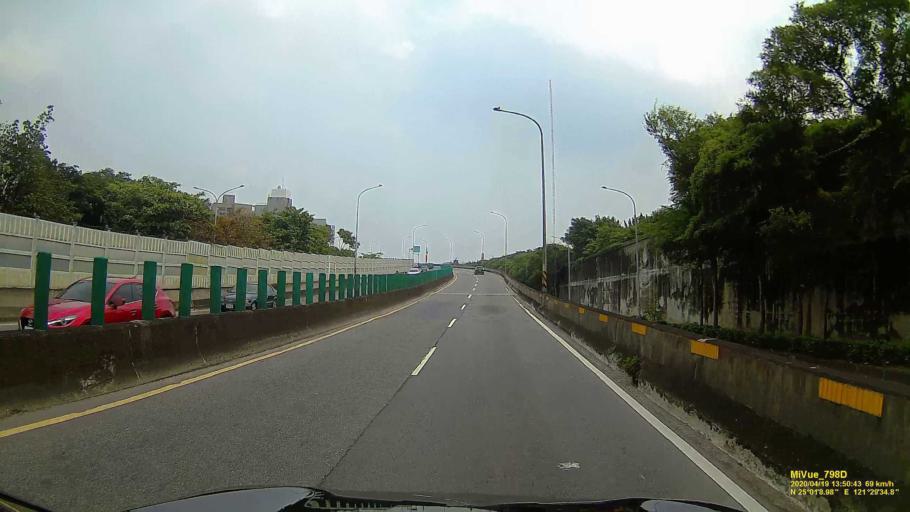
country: TW
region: Taipei
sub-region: Taipei
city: Banqiao
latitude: 25.0188
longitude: 121.4932
